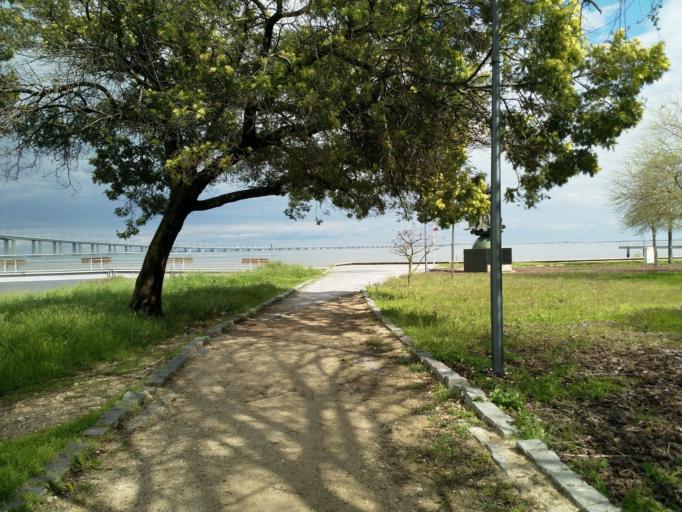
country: PT
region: Lisbon
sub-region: Loures
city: Moscavide
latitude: 38.7816
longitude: -9.0915
